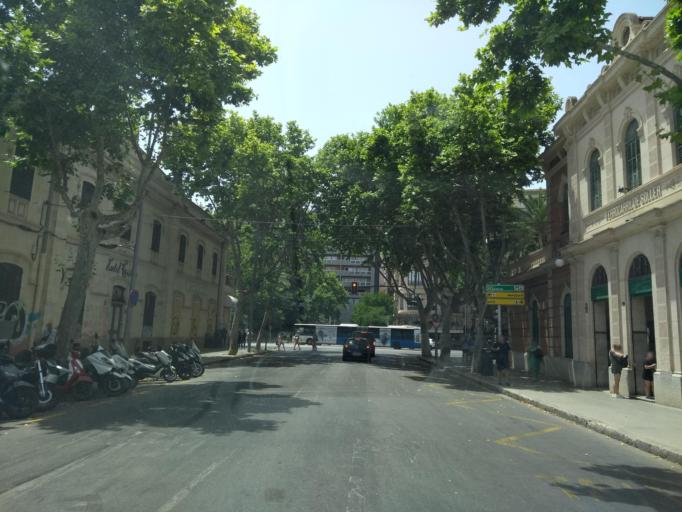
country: ES
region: Balearic Islands
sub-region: Illes Balears
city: Palma
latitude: 39.5768
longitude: 2.6541
